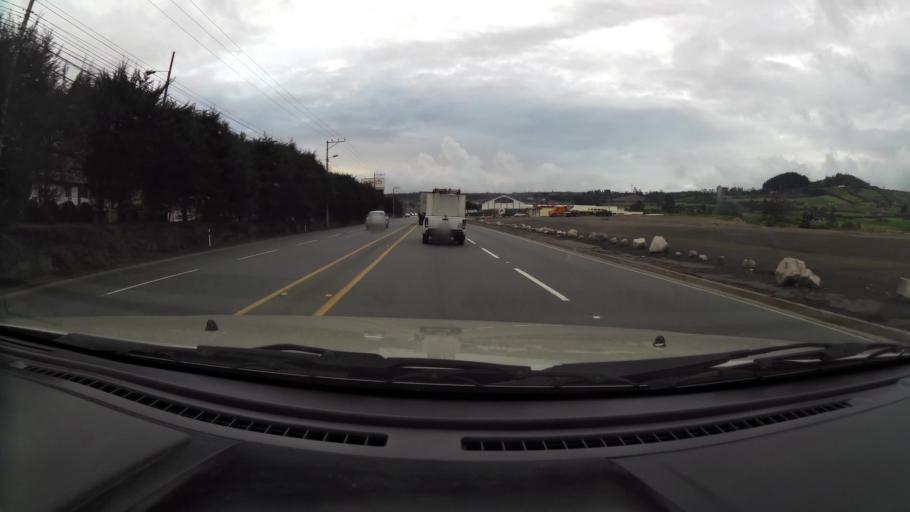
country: EC
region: Pichincha
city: Machachi
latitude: -0.4507
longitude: -78.6390
